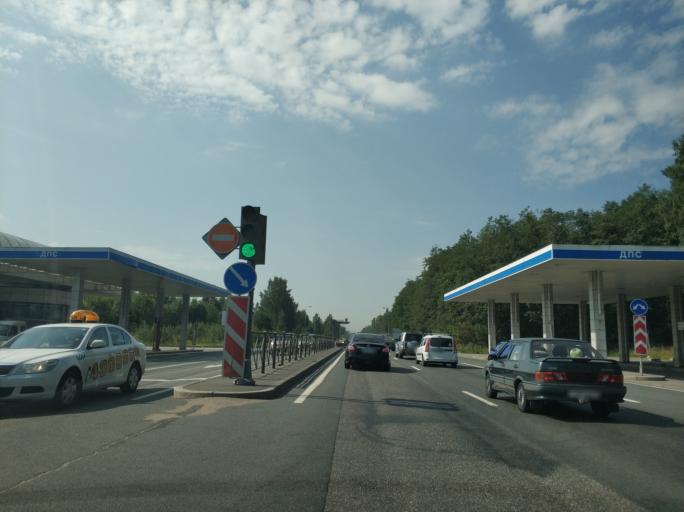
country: RU
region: St.-Petersburg
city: Krasnogvargeisky
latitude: 59.9943
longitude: 30.5389
